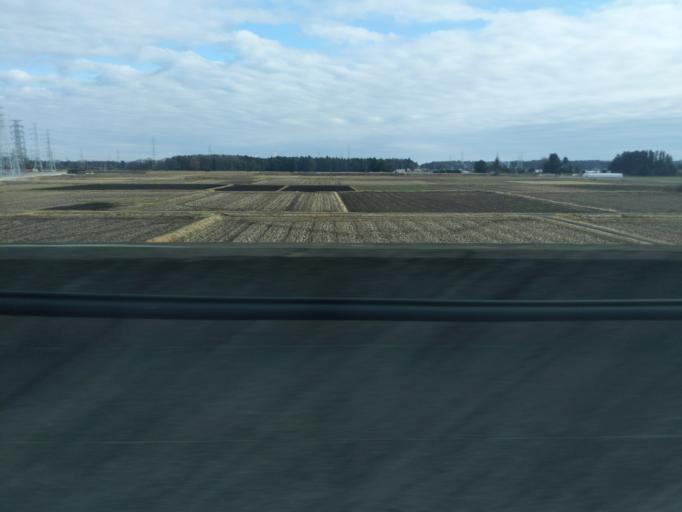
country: JP
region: Tochigi
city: Ujiie
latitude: 36.6519
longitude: 139.9126
